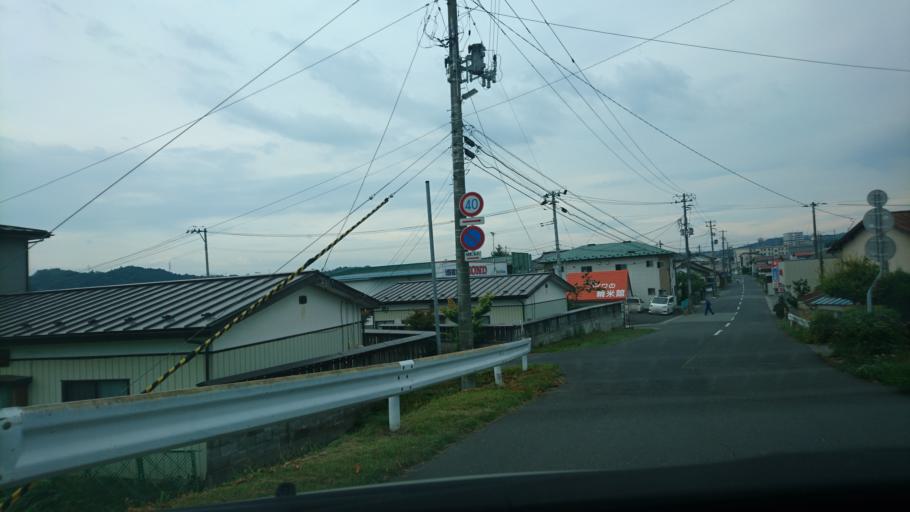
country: JP
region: Iwate
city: Ichinoseki
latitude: 38.9347
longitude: 141.1457
